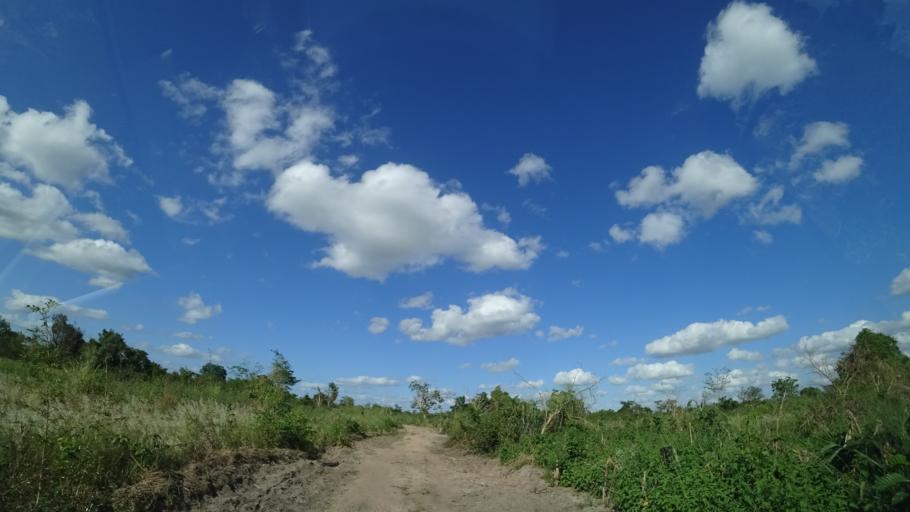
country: MZ
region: Sofala
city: Dondo
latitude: -19.4223
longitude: 34.7141
